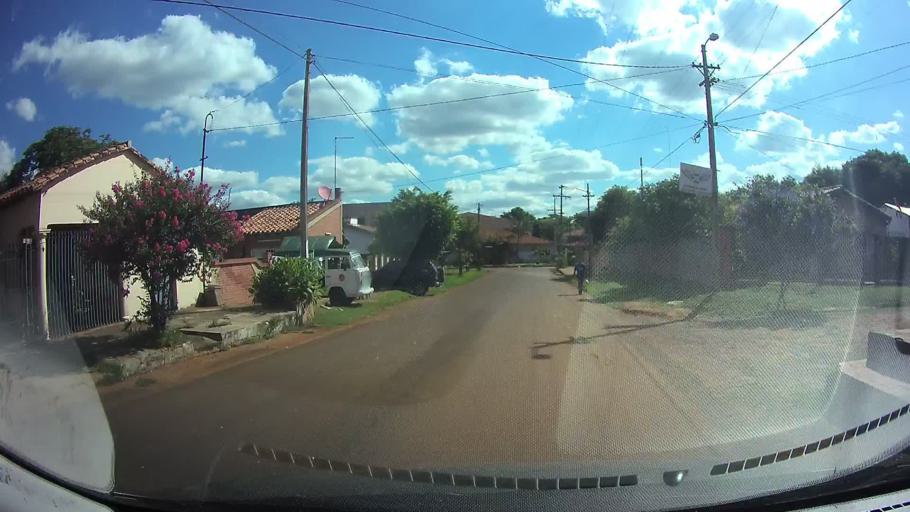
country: PY
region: Central
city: Itaugua
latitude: -25.3905
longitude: -57.3507
